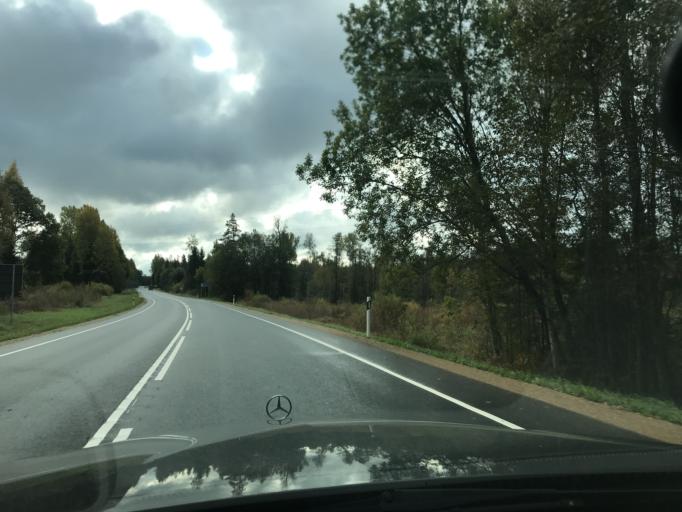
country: EE
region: Viljandimaa
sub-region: Karksi vald
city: Karksi-Nuia
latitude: 58.0349
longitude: 25.6457
